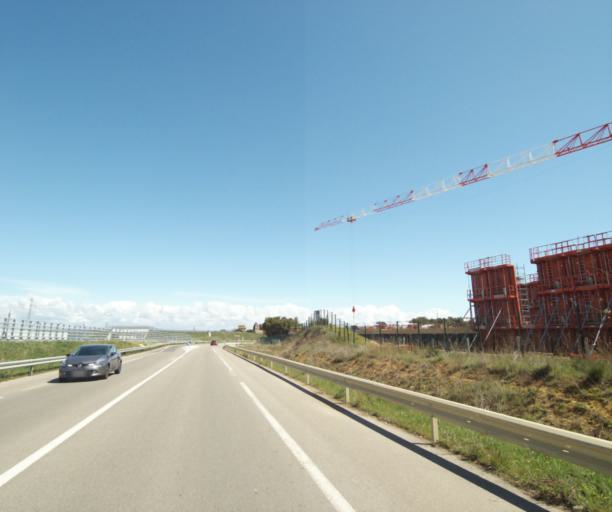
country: FR
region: Languedoc-Roussillon
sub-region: Departement de l'Herault
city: Lattes
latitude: 43.5713
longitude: 3.8762
